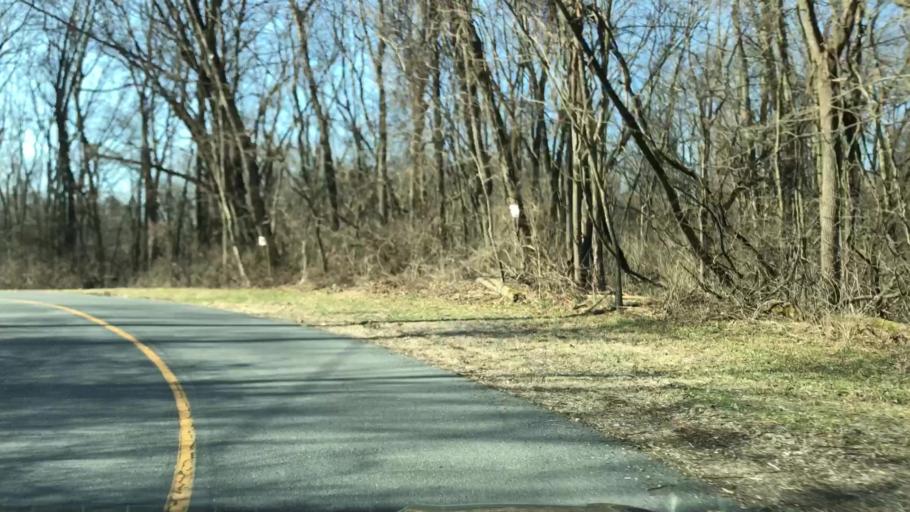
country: US
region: Pennsylvania
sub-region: Dauphin County
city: Highspire
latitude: 40.2201
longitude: -76.7962
